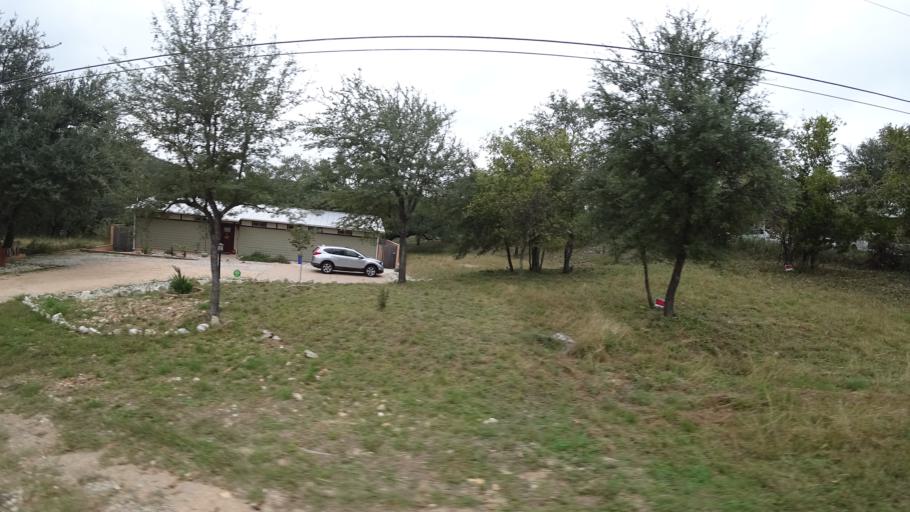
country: US
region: Texas
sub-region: Travis County
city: Bee Cave
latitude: 30.3303
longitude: -97.9257
